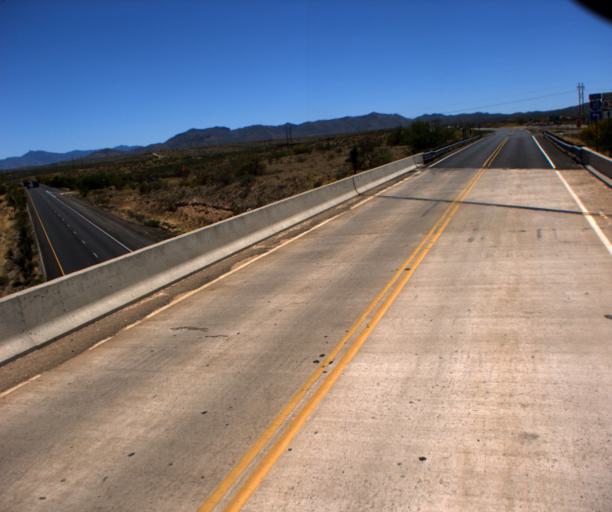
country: US
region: Arizona
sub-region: Pima County
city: Vail
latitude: 32.0068
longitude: -110.6902
